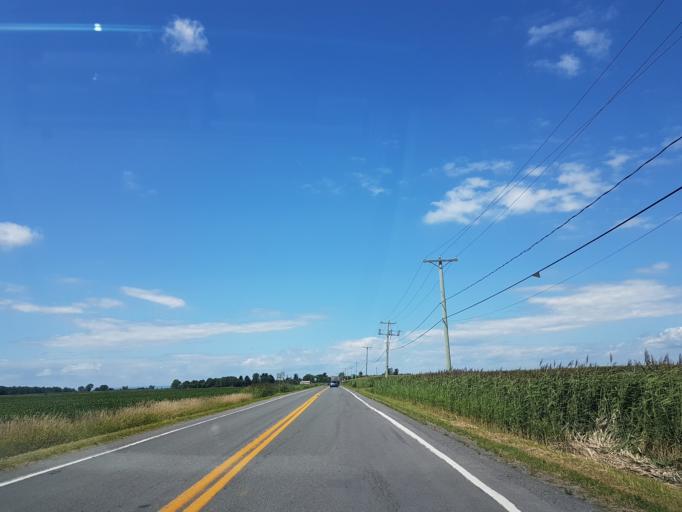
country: CA
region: Quebec
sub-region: Mauricie
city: Nicolet
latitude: 46.1231
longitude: -72.6950
